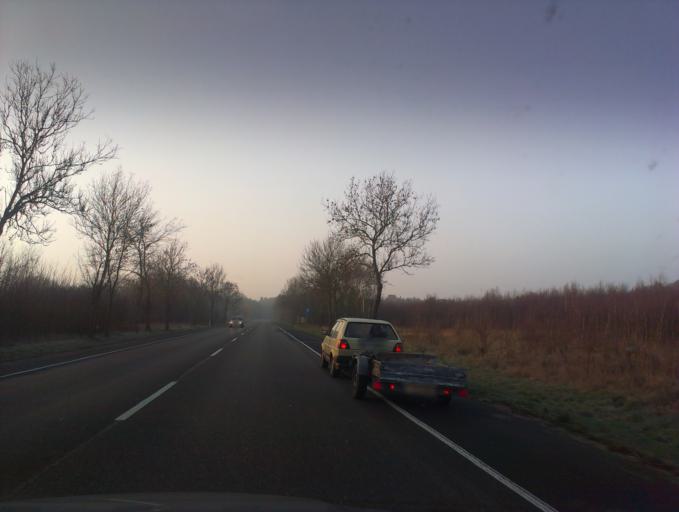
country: PL
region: Greater Poland Voivodeship
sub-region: Powiat obornicki
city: Rogozno
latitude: 52.7295
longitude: 16.9389
